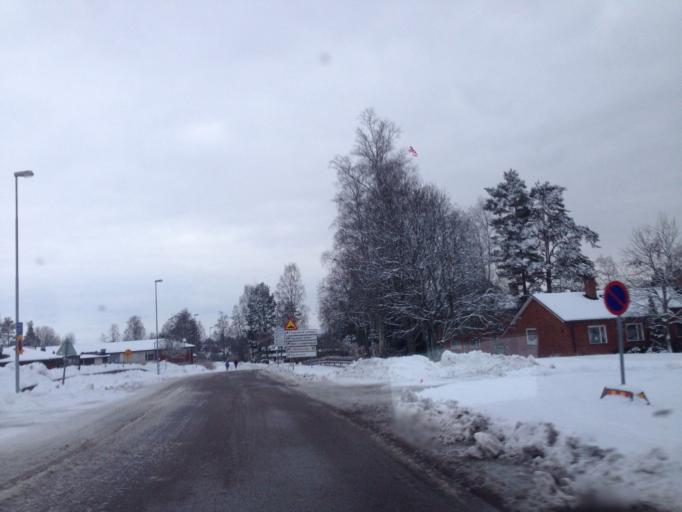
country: SE
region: Dalarna
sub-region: Mora Kommun
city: Mora
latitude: 61.0158
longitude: 14.5872
